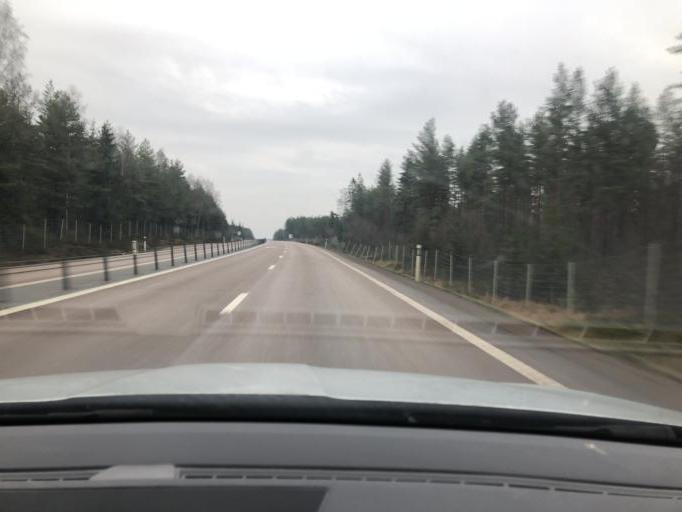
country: SE
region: Vaermland
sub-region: Kristinehamns Kommun
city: Bjorneborg
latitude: 59.3117
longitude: 14.2307
